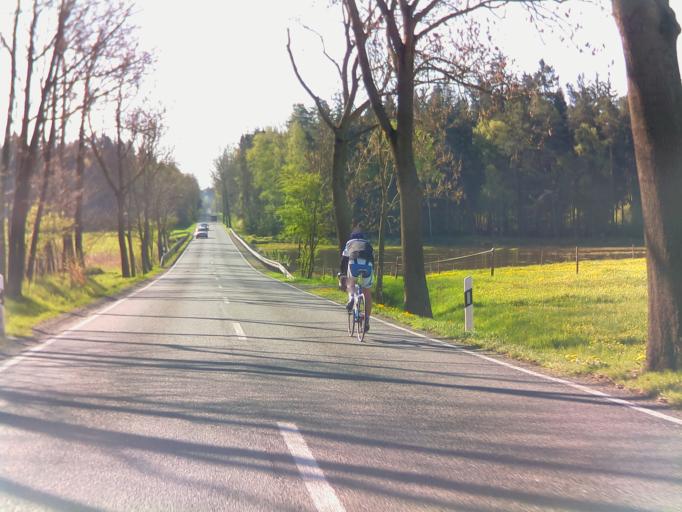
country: DE
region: Thuringia
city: Mossbach
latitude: 50.6772
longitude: 11.7841
